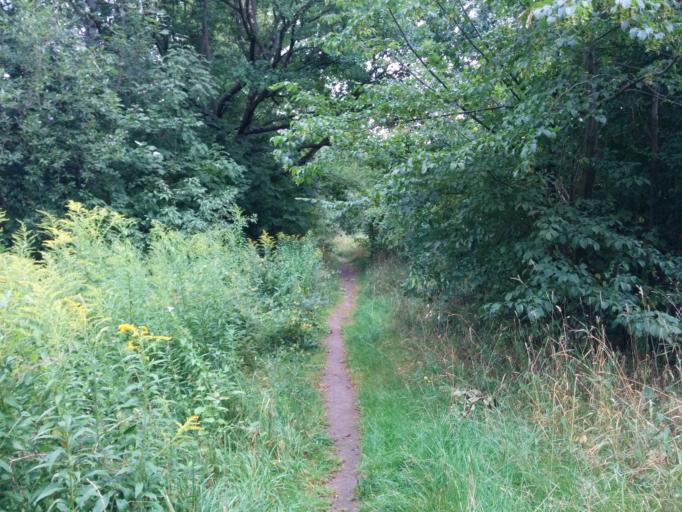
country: DE
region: Saxony
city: Neukirchen
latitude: 50.7991
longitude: 12.8892
